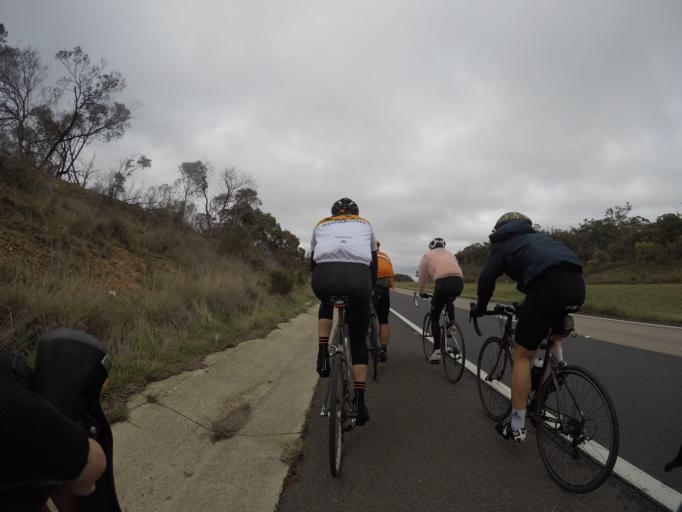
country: AU
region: New South Wales
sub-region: Lithgow
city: Lithgow
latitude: -33.4354
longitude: 150.0702
